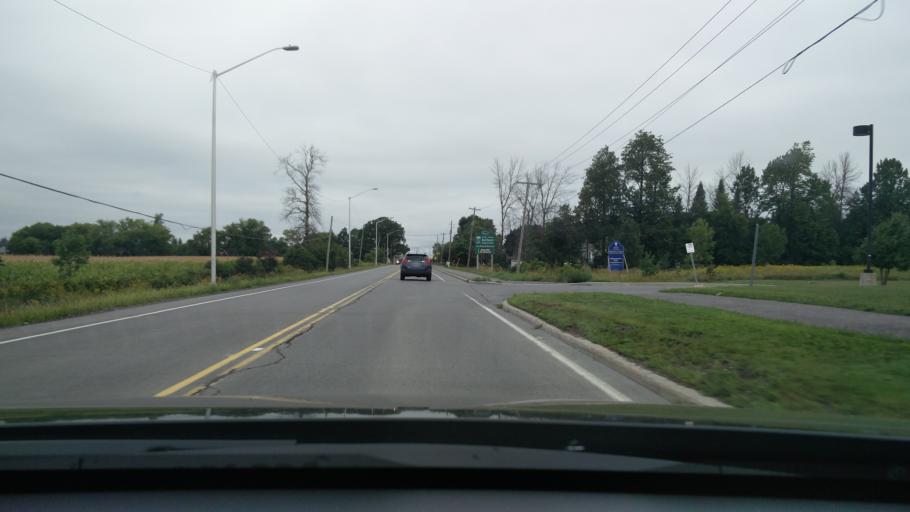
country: CA
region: Ontario
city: Bells Corners
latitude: 45.2626
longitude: -75.7417
